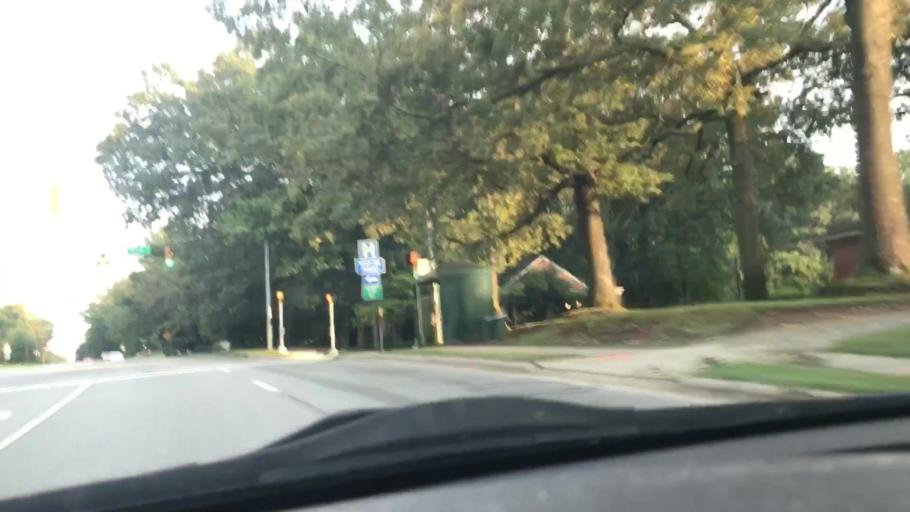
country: US
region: North Carolina
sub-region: Guilford County
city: Greensboro
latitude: 36.0817
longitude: -79.8291
